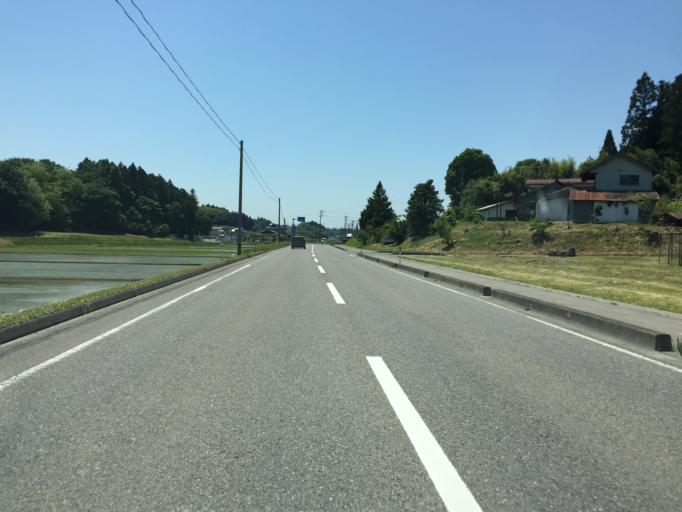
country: JP
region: Fukushima
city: Motomiya
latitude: 37.5048
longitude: 140.4577
